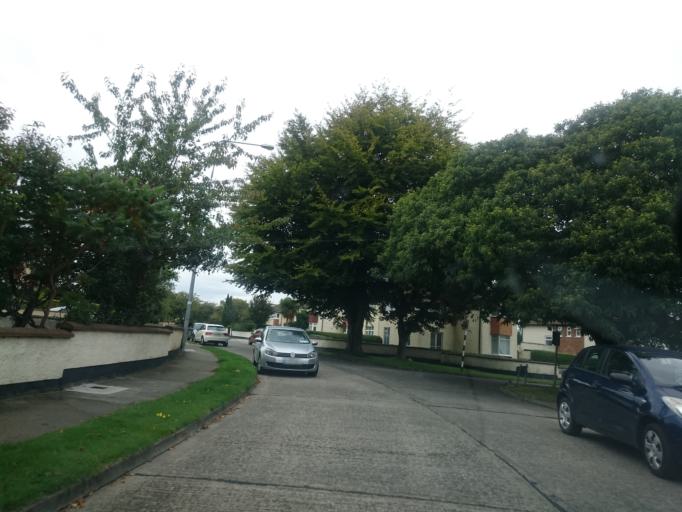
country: IE
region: Leinster
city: Mount Merrion
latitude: 53.3077
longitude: -6.2111
